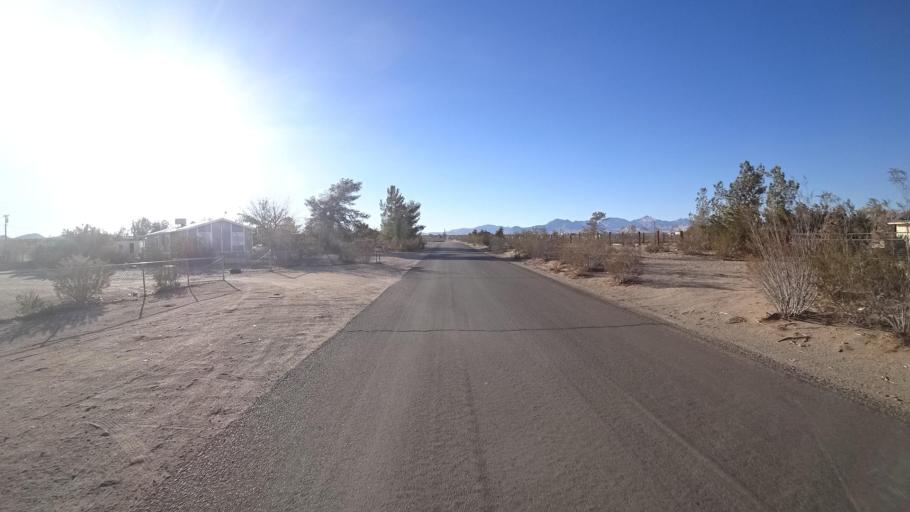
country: US
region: California
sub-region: Kern County
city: Ridgecrest
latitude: 35.6006
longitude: -117.7108
